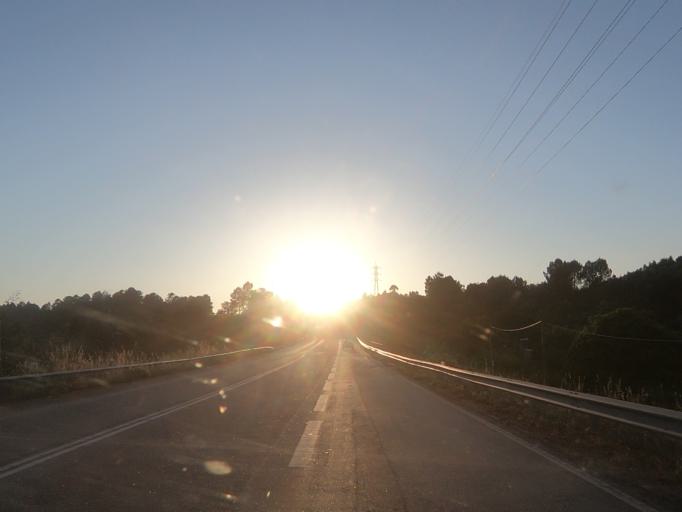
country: PT
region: Viseu
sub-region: Viseu
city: Rio de Loba
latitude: 40.6818
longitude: -7.8850
